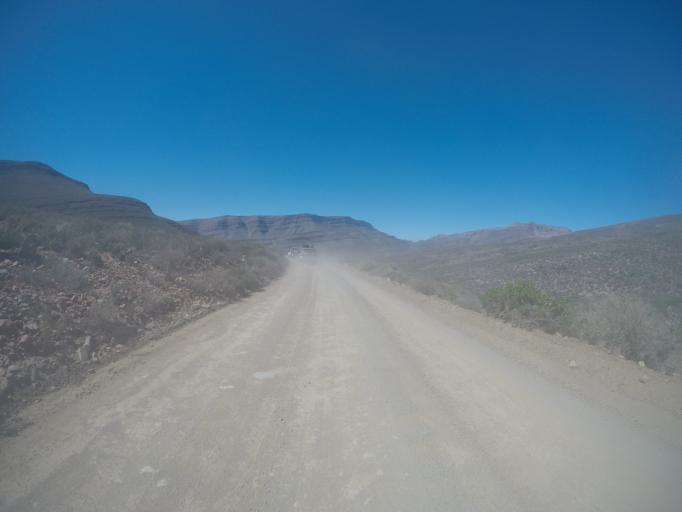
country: ZA
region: Western Cape
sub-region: West Coast District Municipality
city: Clanwilliam
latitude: -32.6208
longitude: 19.3847
